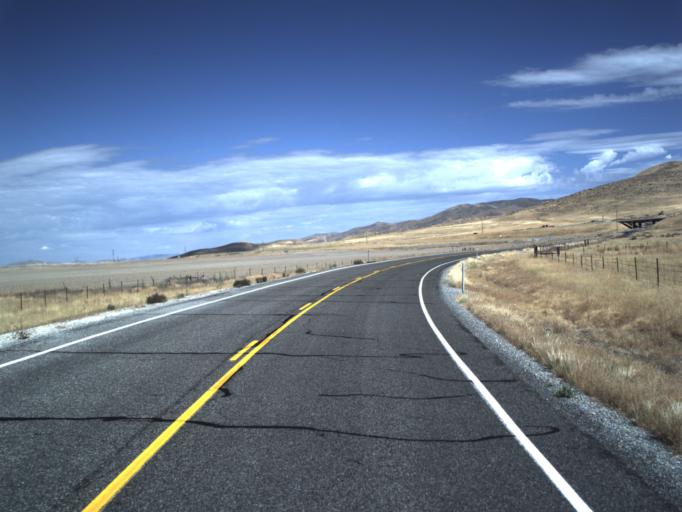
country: US
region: Utah
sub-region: Box Elder County
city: Garland
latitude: 41.8096
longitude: -112.4165
